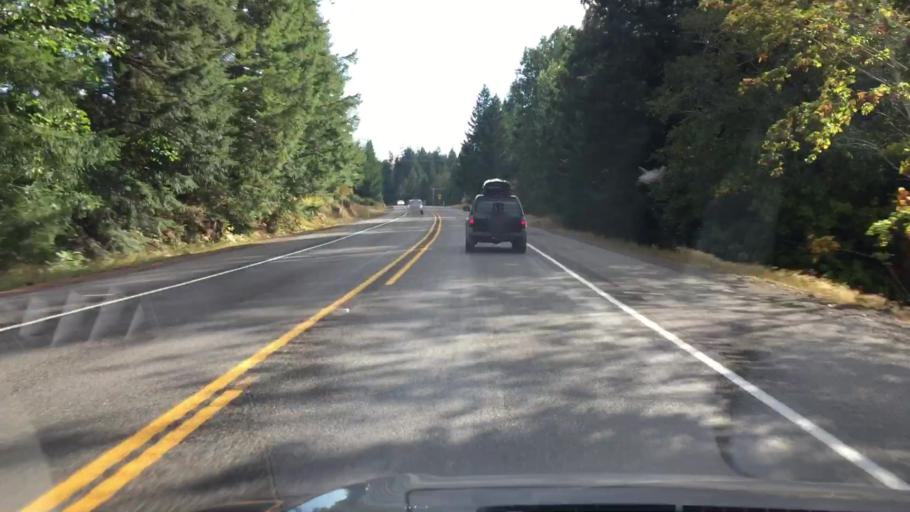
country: US
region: Washington
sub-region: Lewis County
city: Morton
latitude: 46.6223
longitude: -121.6600
